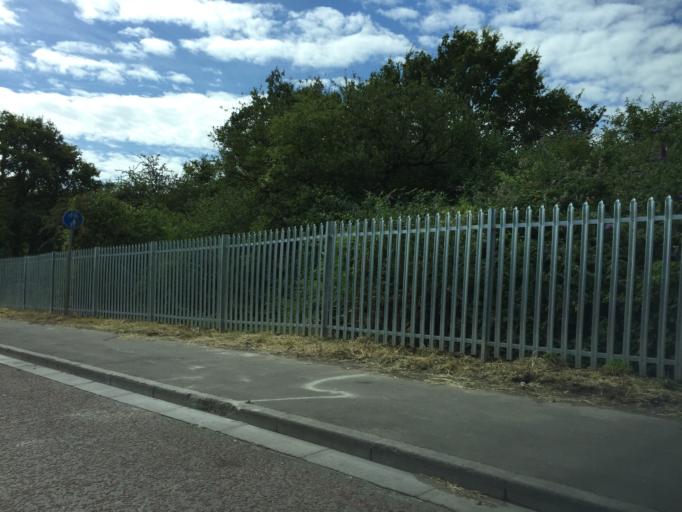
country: GB
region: Wales
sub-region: Newport
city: Nash
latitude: 51.5655
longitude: -2.9686
